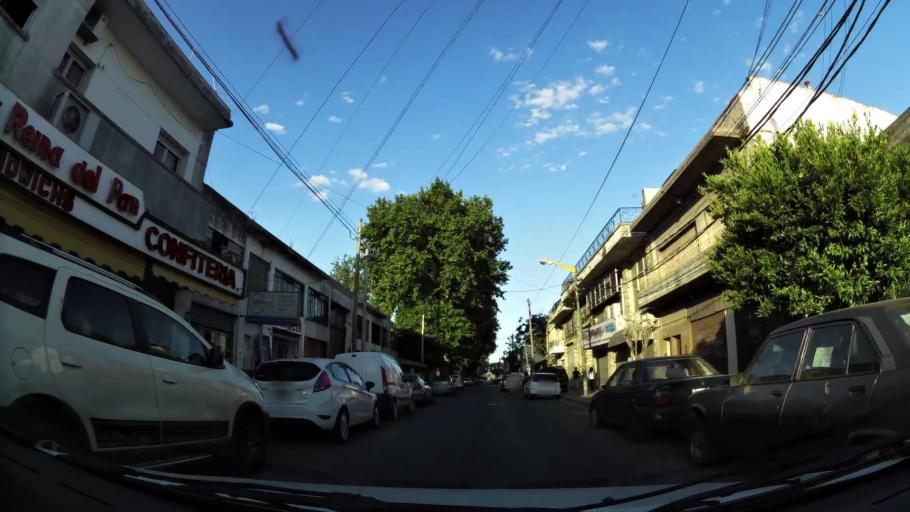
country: AR
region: Buenos Aires
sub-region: Partido de General San Martin
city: General San Martin
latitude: -34.5689
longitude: -58.5220
